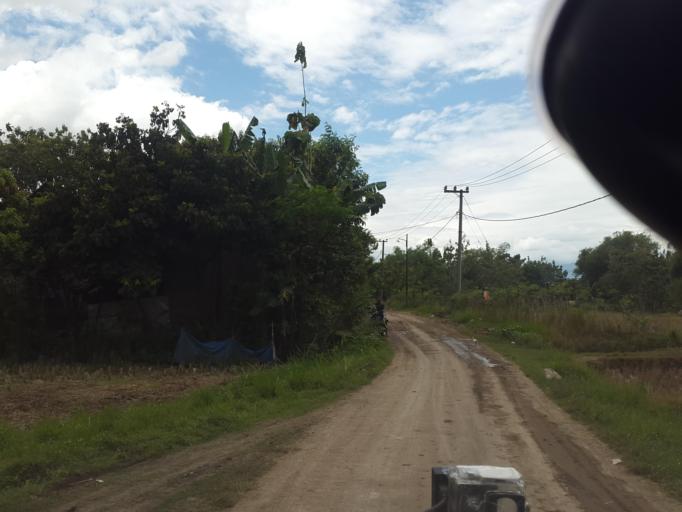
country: ID
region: East Java
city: Madiun
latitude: -7.5594
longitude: 111.6917
